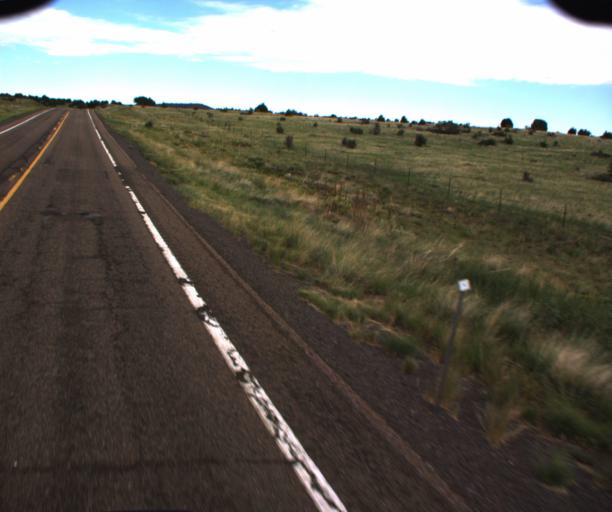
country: US
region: Arizona
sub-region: Apache County
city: Springerville
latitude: 34.2478
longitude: -109.5316
